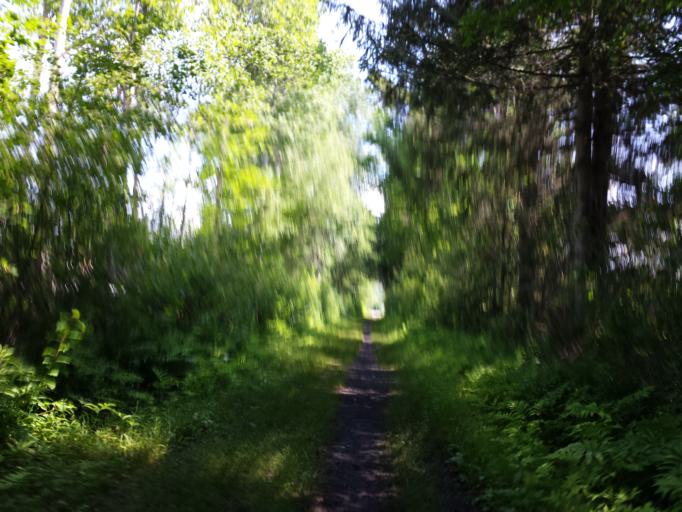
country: US
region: Vermont
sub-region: Rutland County
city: Castleton
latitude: 43.6043
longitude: -73.1805
